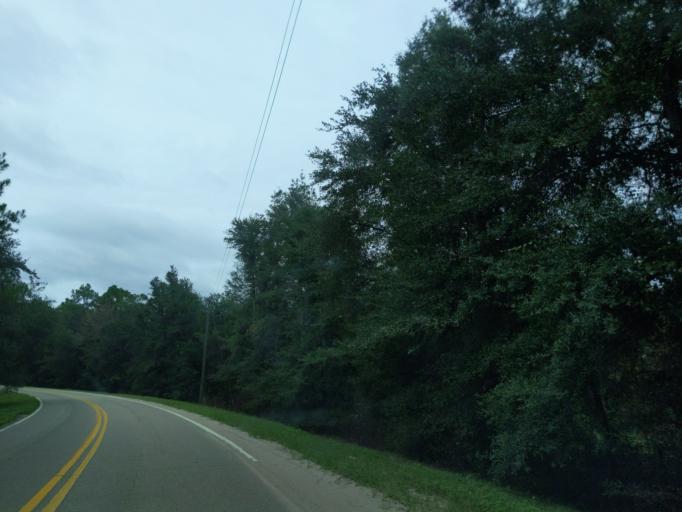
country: US
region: Florida
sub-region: Gadsden County
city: Midway
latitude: 30.4242
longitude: -84.4126
